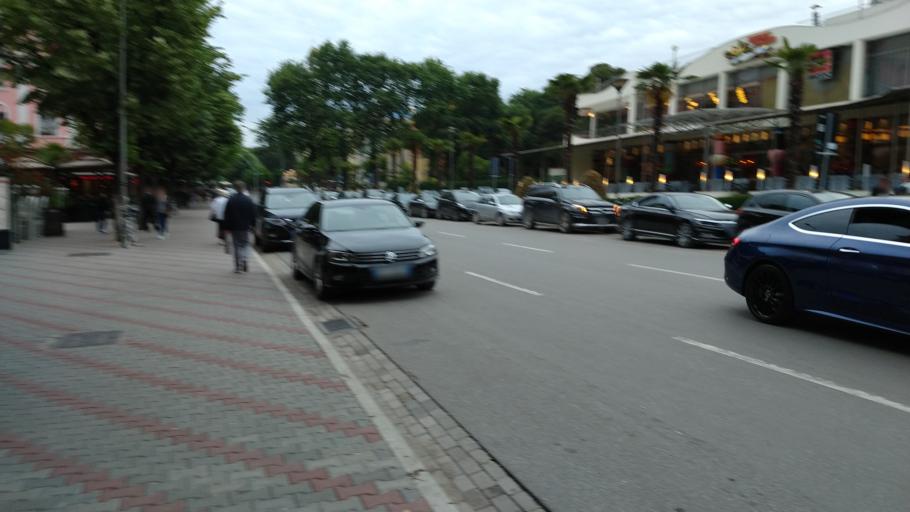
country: AL
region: Tirane
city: Tirana
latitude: 41.3243
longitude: 19.8172
